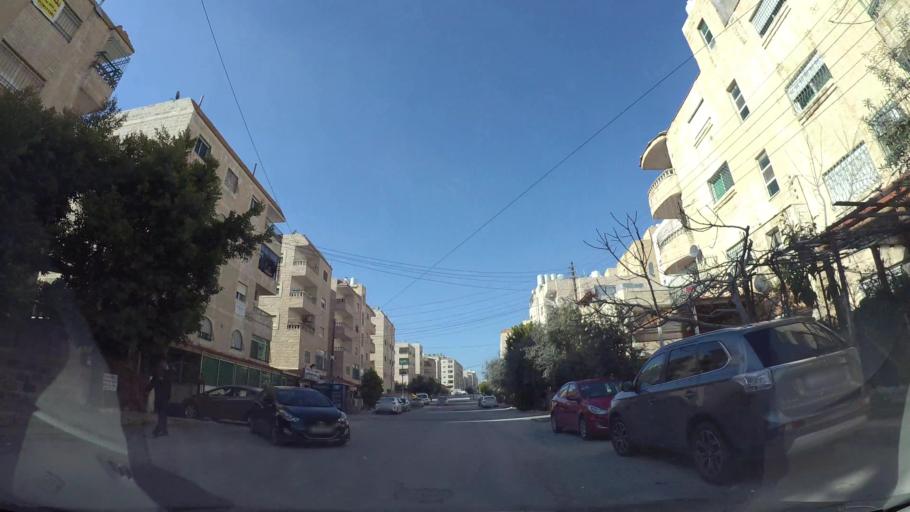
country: JO
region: Amman
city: Amman
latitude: 31.9804
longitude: 35.9341
